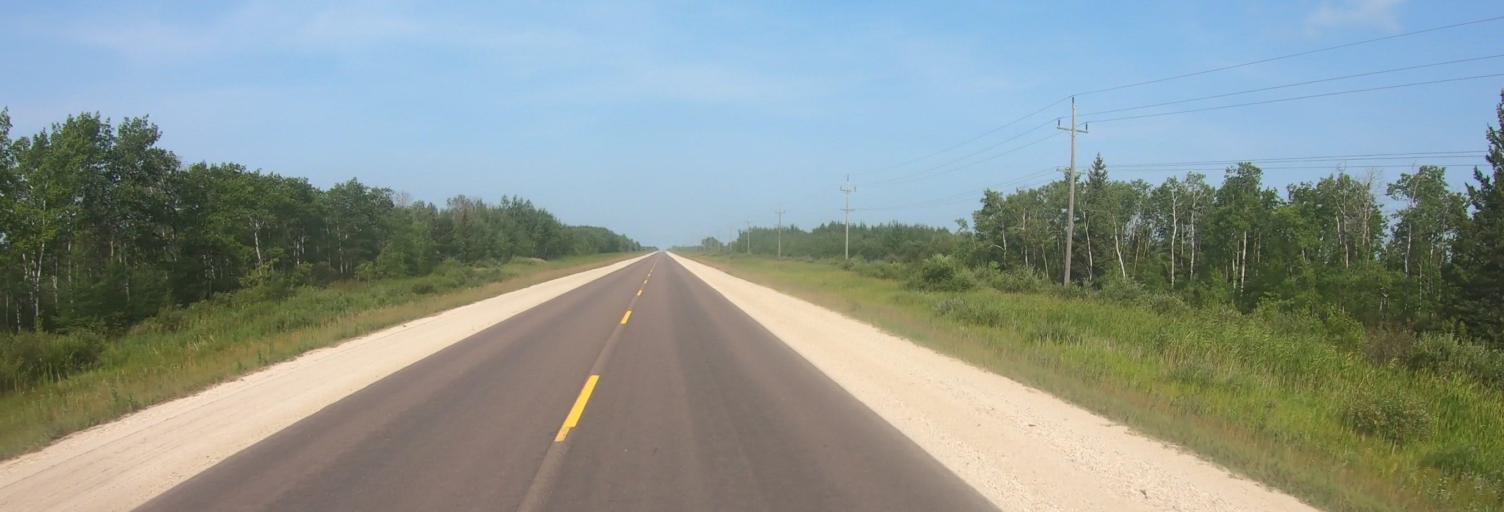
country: CA
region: Manitoba
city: La Broquerie
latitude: 49.2691
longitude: -96.4793
